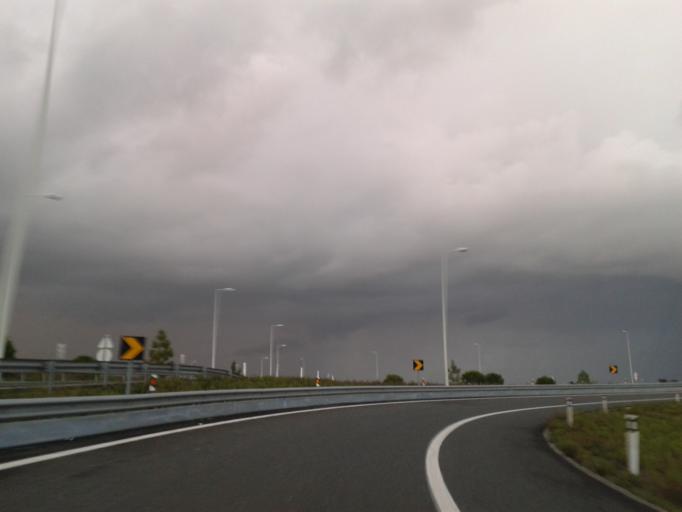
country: PT
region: Santarem
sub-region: Benavente
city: Poceirao
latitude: 38.8369
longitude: -8.7283
